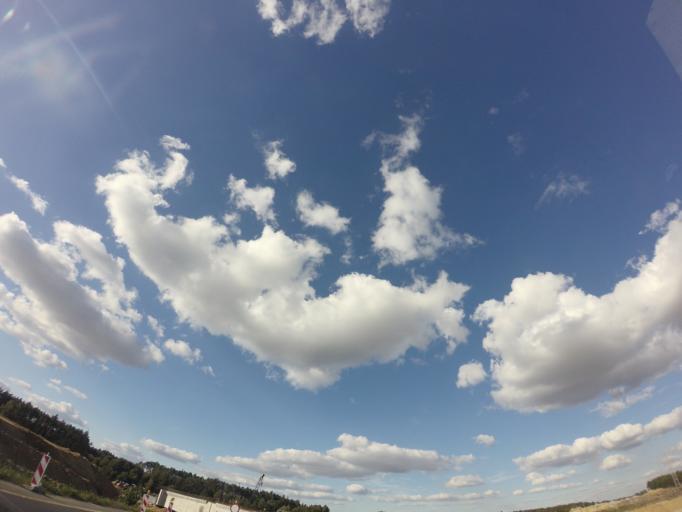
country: PL
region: Greater Poland Voivodeship
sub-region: Powiat leszczynski
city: Lipno
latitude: 51.9453
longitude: 16.5464
